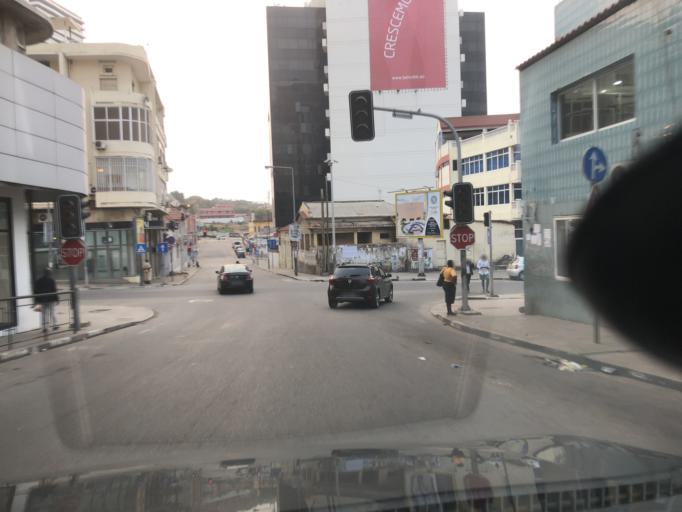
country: AO
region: Luanda
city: Luanda
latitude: -8.8166
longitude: 13.2323
